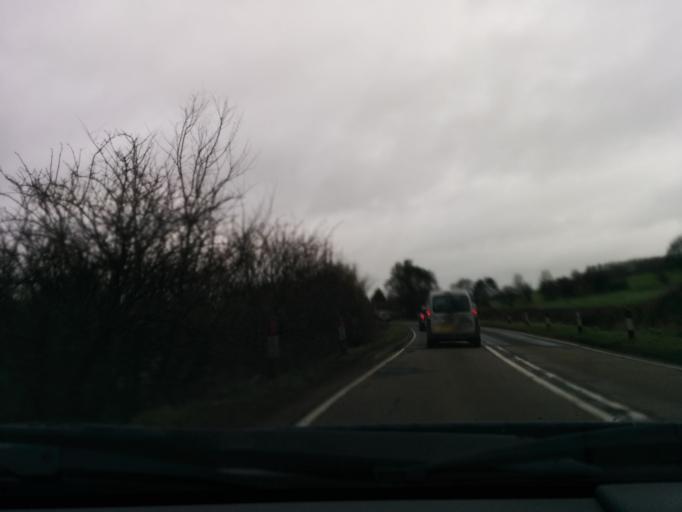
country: GB
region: England
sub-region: Oxfordshire
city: Eynsham
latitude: 51.7694
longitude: -1.3580
